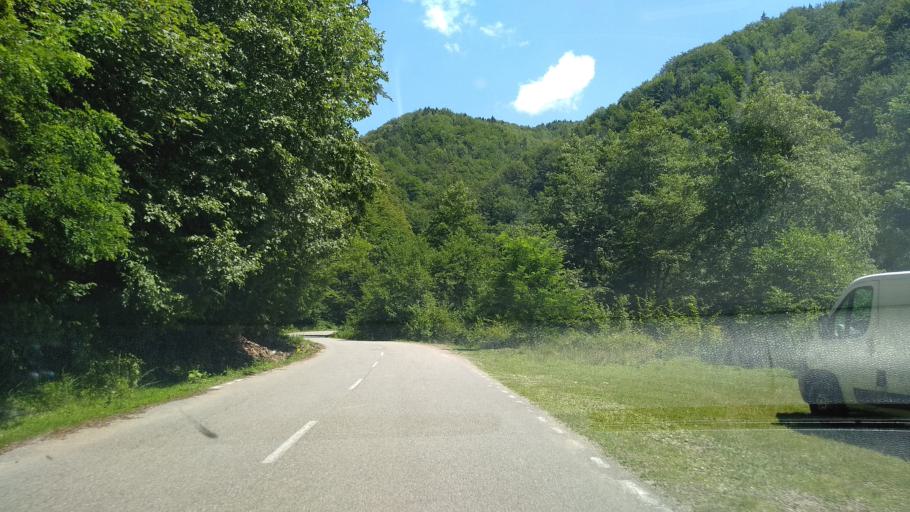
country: RO
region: Hunedoara
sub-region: Comuna Orastioara de Sus
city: Orastioara de Sus
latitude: 45.6209
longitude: 23.2330
